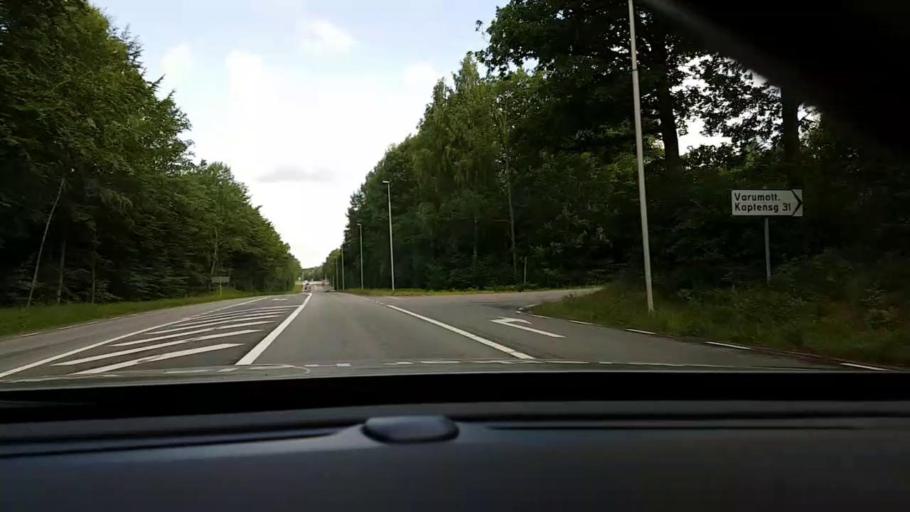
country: SE
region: Skane
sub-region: Hassleholms Kommun
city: Hassleholm
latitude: 56.1605
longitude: 13.7399
